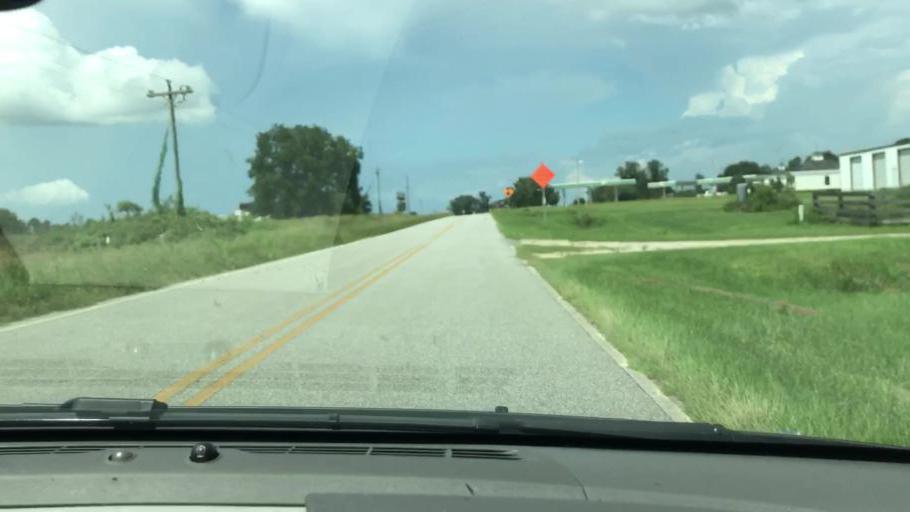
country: US
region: Georgia
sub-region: Seminole County
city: Donalsonville
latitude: 31.0884
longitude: -84.9959
